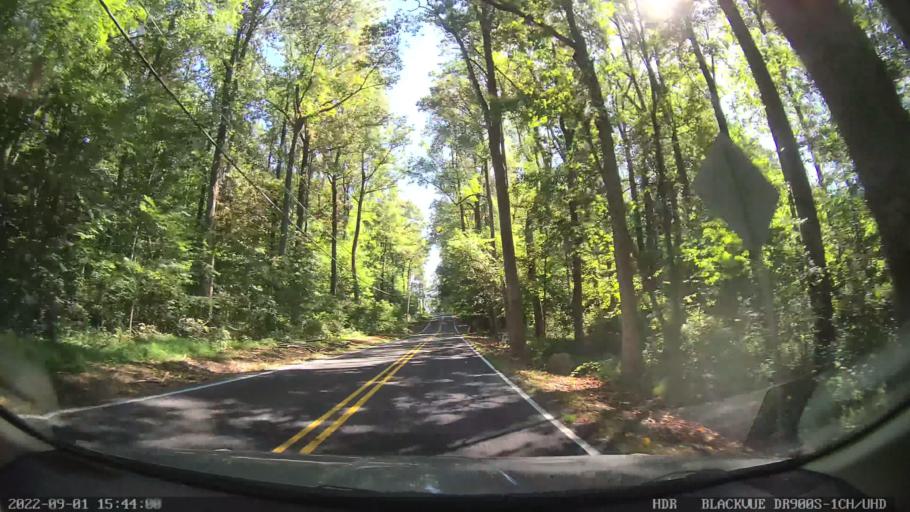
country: US
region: Pennsylvania
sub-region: Berks County
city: Topton
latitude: 40.4758
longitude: -75.7000
